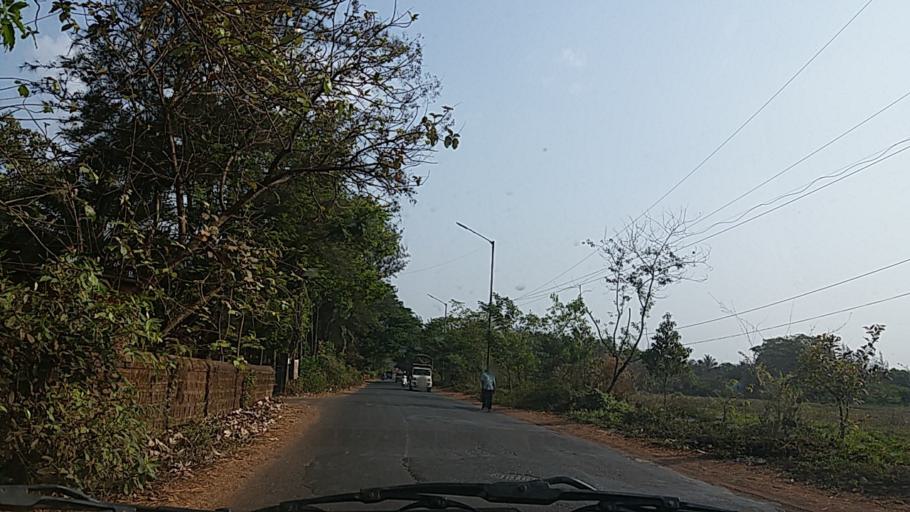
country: IN
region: Goa
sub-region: South Goa
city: Madgaon
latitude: 15.2633
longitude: 73.9701
